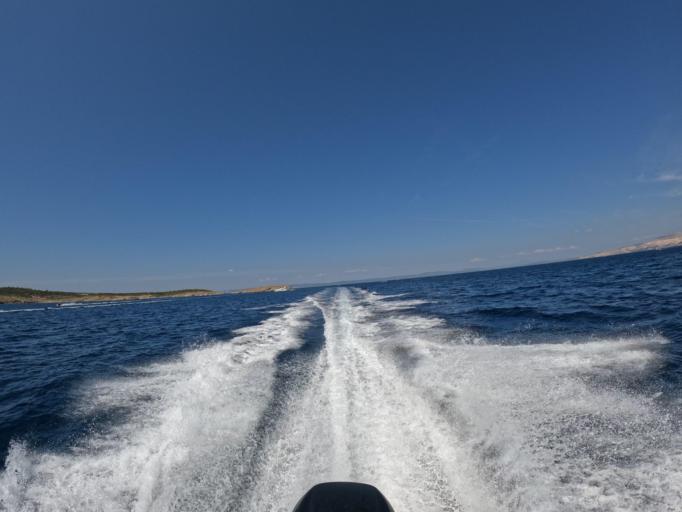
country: HR
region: Primorsko-Goranska
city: Lopar
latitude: 44.8537
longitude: 14.7373
